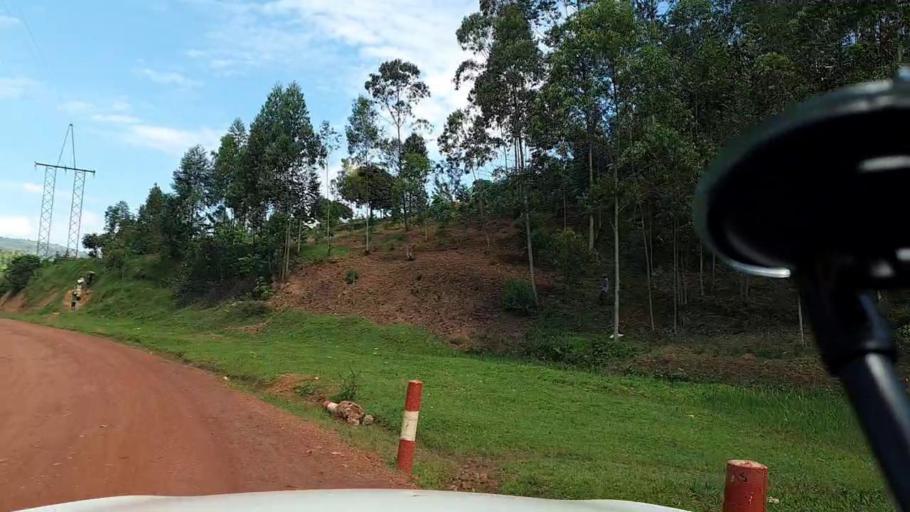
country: RW
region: Kigali
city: Kigali
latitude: -1.7940
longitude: 29.8874
